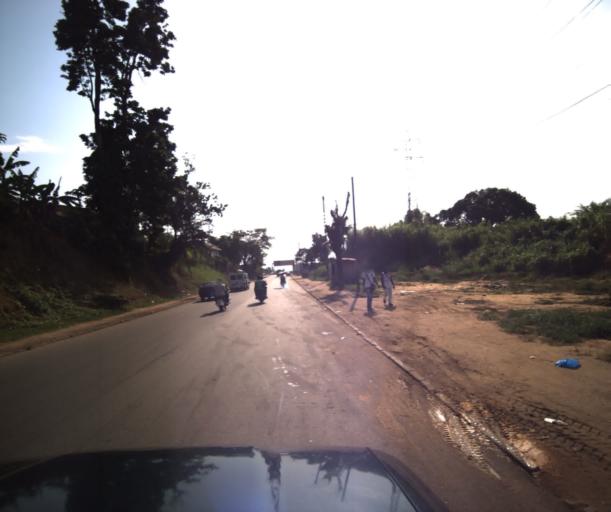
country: CM
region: Littoral
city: Bonaberi
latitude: 4.0708
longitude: 9.6888
